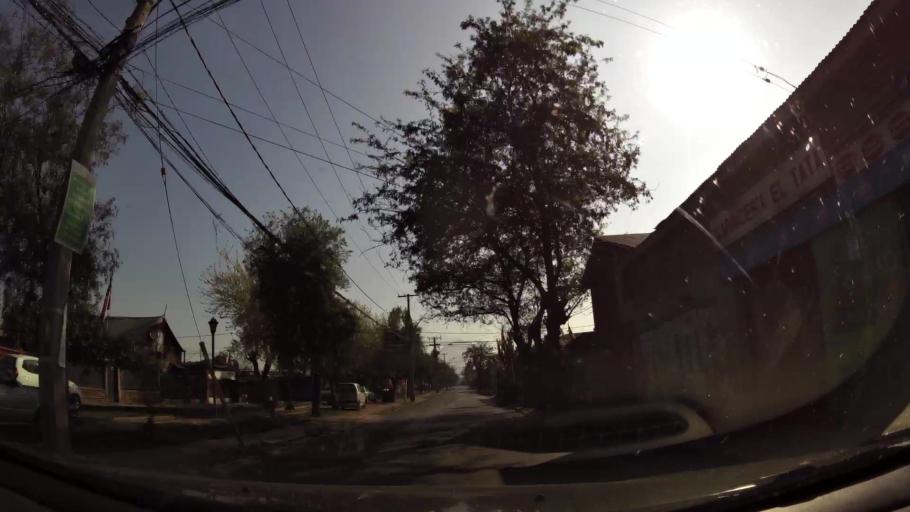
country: CL
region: Santiago Metropolitan
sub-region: Provincia de Santiago
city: Santiago
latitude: -33.3836
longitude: -70.6682
